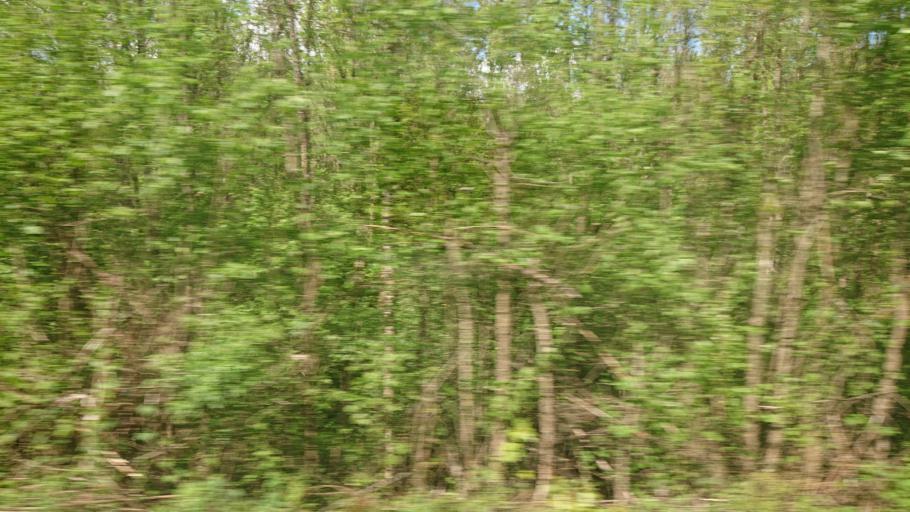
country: FR
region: Rhone-Alpes
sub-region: Departement de l'Ain
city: Artemare
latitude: 45.8629
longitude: 5.7026
